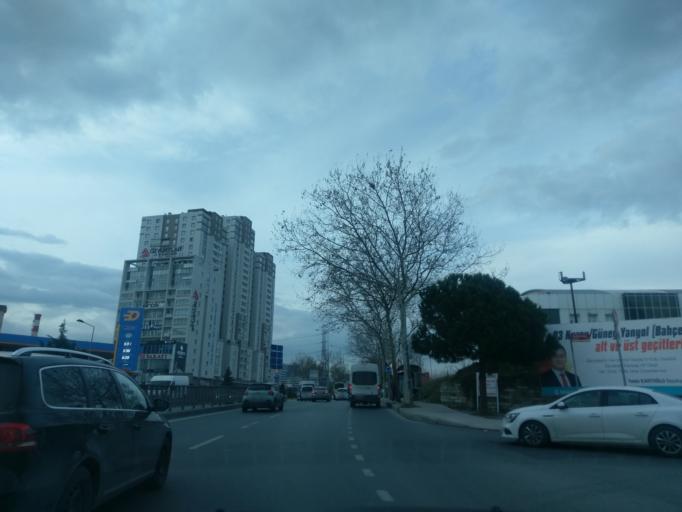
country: TR
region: Istanbul
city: Esenyurt
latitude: 41.0645
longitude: 28.6730
